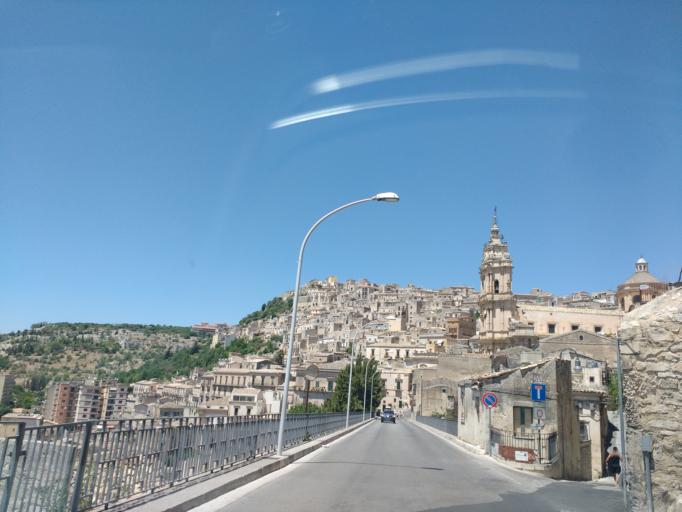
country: IT
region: Sicily
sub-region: Ragusa
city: Modica
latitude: 36.8625
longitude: 14.7614
